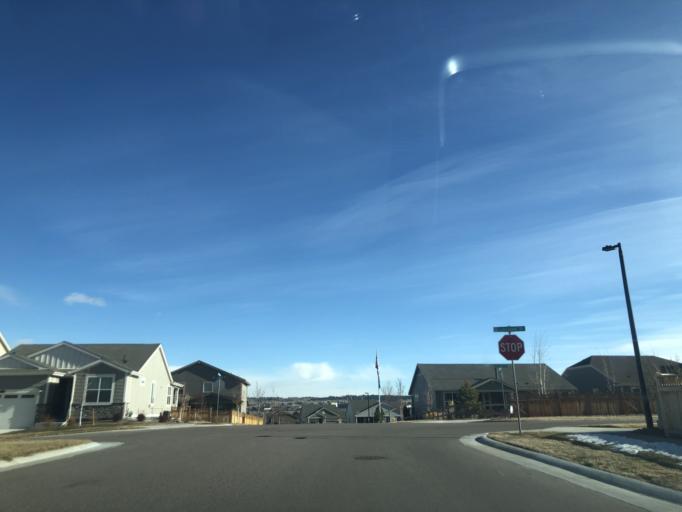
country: US
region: Colorado
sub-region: Douglas County
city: Stonegate
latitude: 39.5550
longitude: -104.8006
